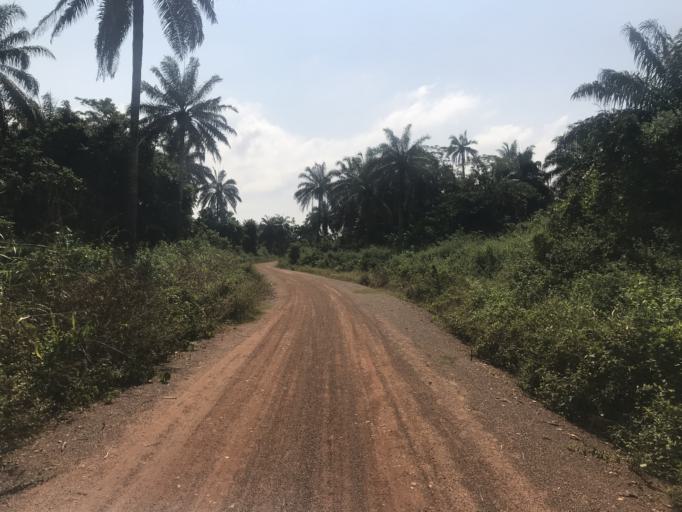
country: NG
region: Osun
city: Ikirun
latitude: 7.8293
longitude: 4.6385
